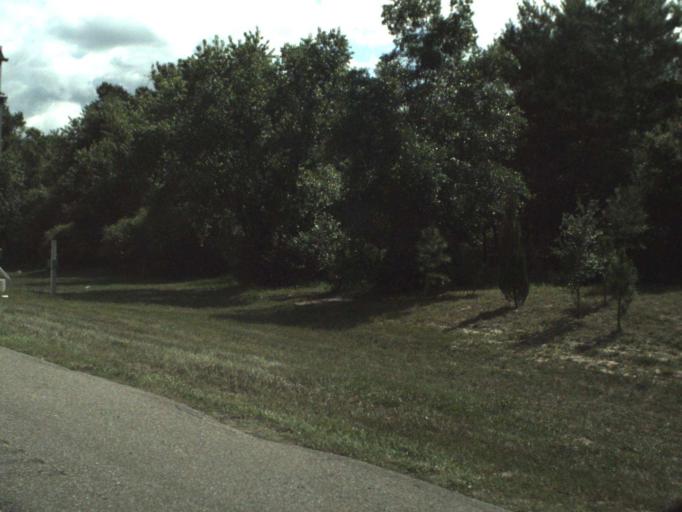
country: US
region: Florida
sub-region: Volusia County
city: Deltona
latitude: 28.9286
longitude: -81.2660
